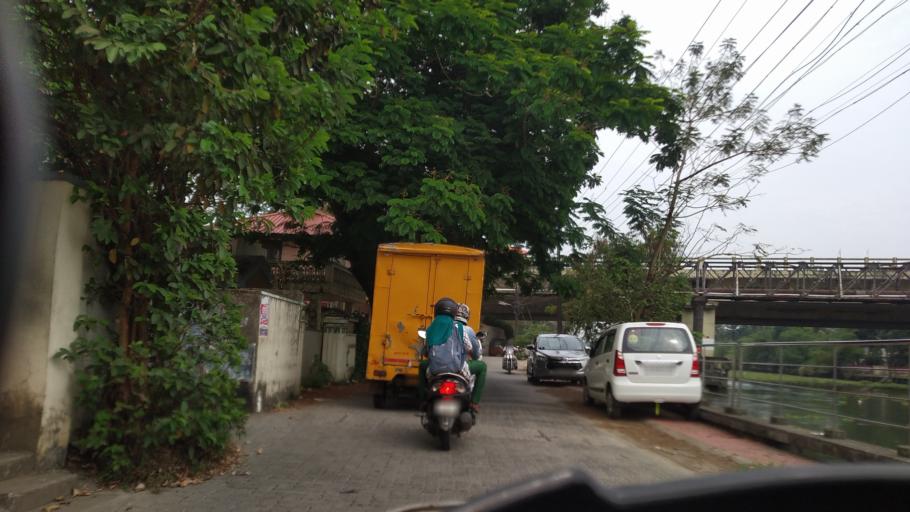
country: IN
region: Kerala
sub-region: Ernakulam
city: Cochin
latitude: 9.9547
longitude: 76.3172
